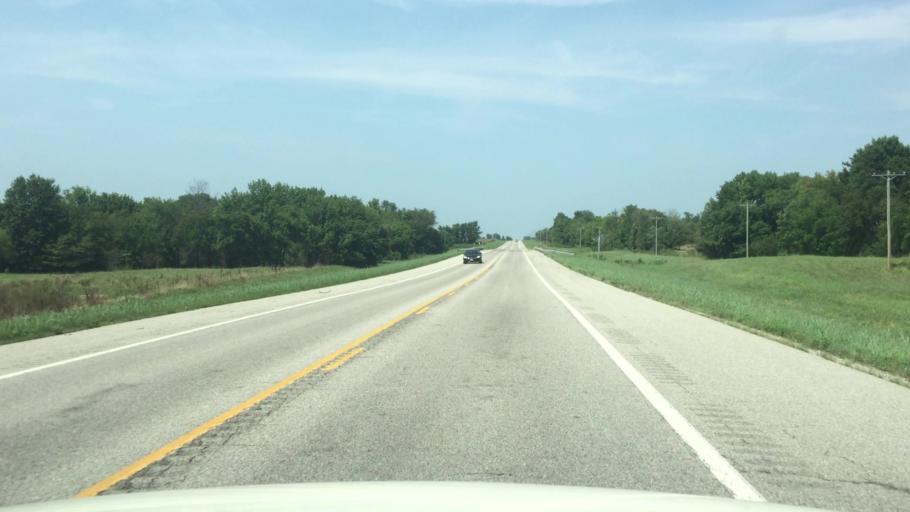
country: US
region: Kansas
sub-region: Crawford County
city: Pittsburg
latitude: 37.2536
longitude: -94.7051
